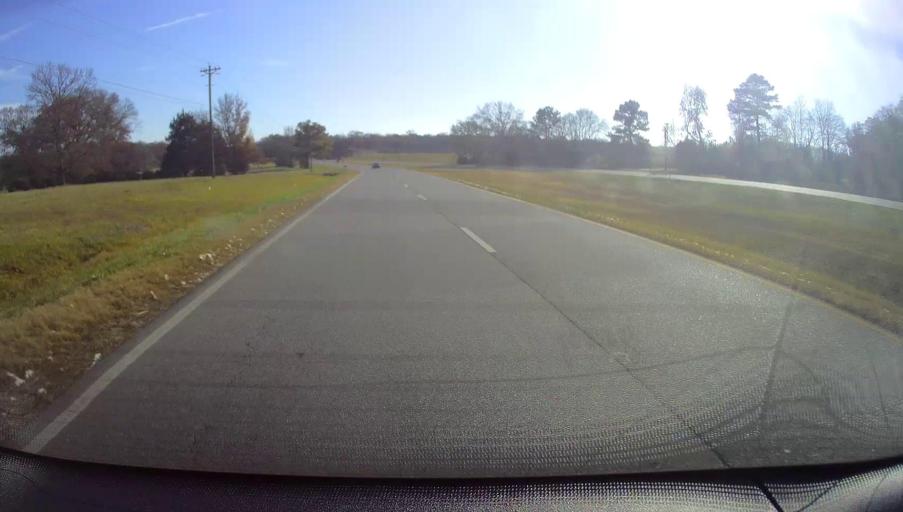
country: US
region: Alabama
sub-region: Morgan County
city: Decatur
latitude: 34.6947
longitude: -86.9555
